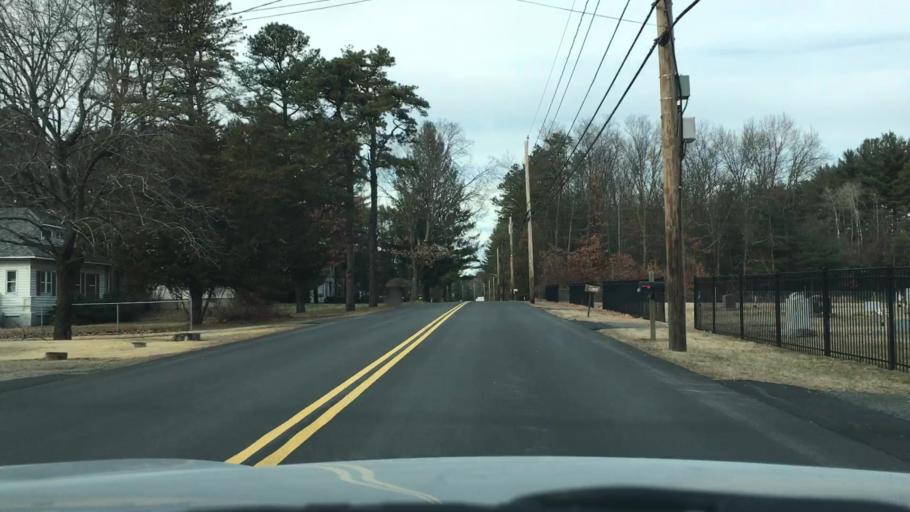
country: US
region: Massachusetts
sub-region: Hampden County
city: Westfield
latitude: 42.1472
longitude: -72.7406
